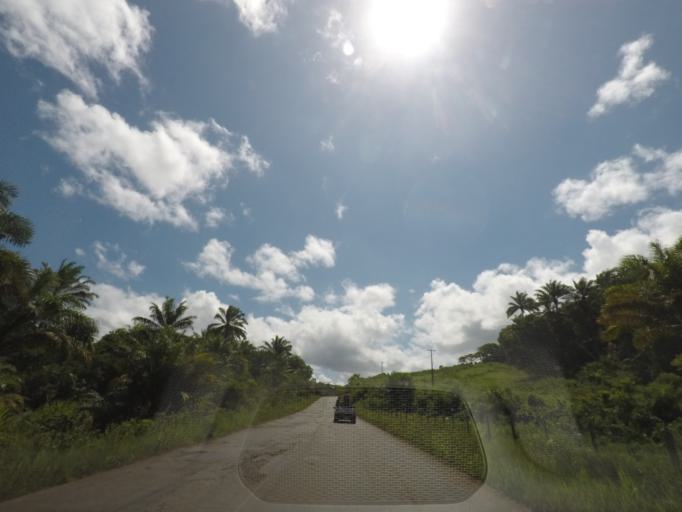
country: BR
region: Bahia
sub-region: Taperoa
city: Taperoa
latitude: -13.5160
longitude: -39.0962
